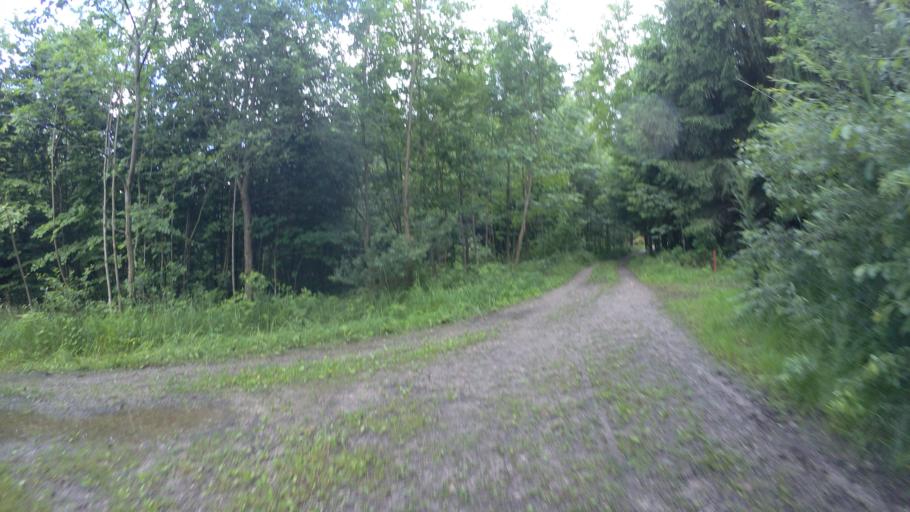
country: DE
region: Bavaria
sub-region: Upper Bavaria
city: Grabenstatt
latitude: 47.8350
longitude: 12.5386
